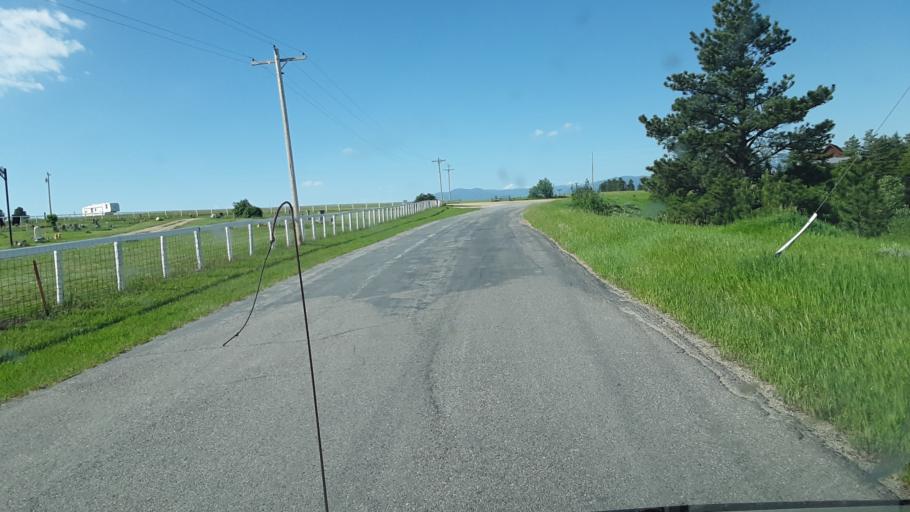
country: US
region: Montana
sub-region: Carbon County
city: Red Lodge
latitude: 45.3612
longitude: -109.1550
